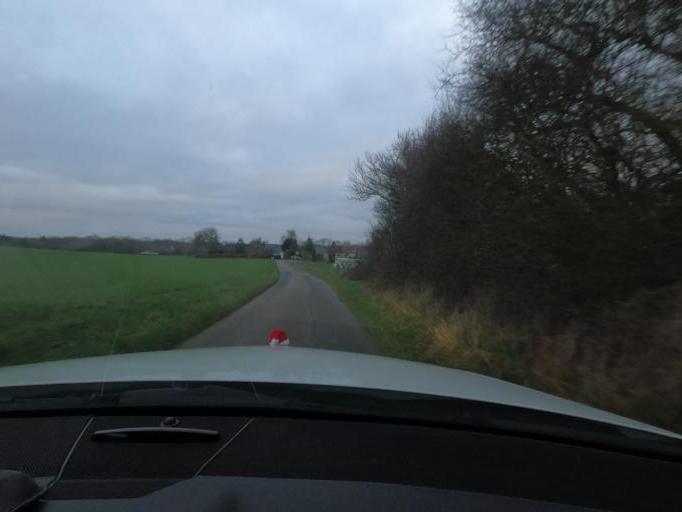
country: DK
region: South Denmark
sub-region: Sonderborg Kommune
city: Sonderborg
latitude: 54.9038
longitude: 9.8501
